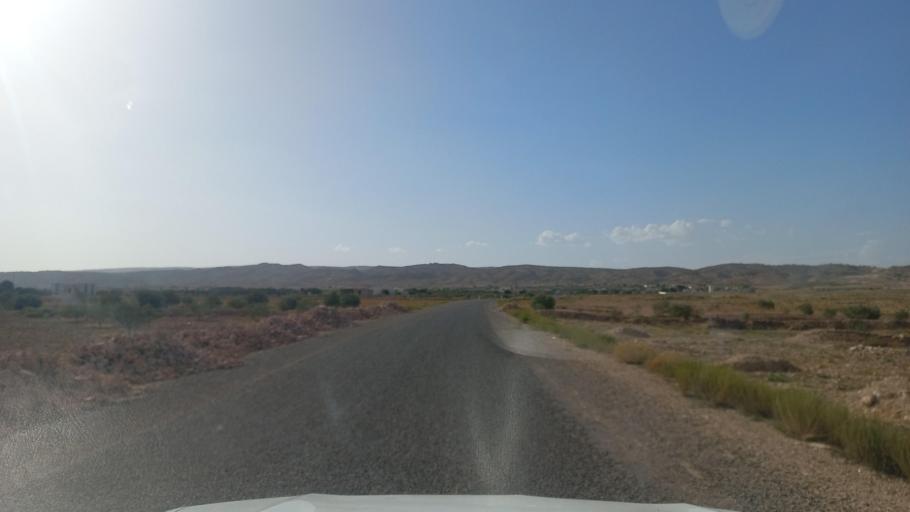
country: TN
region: Al Qasrayn
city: Sbiba
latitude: 35.3392
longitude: 8.9968
